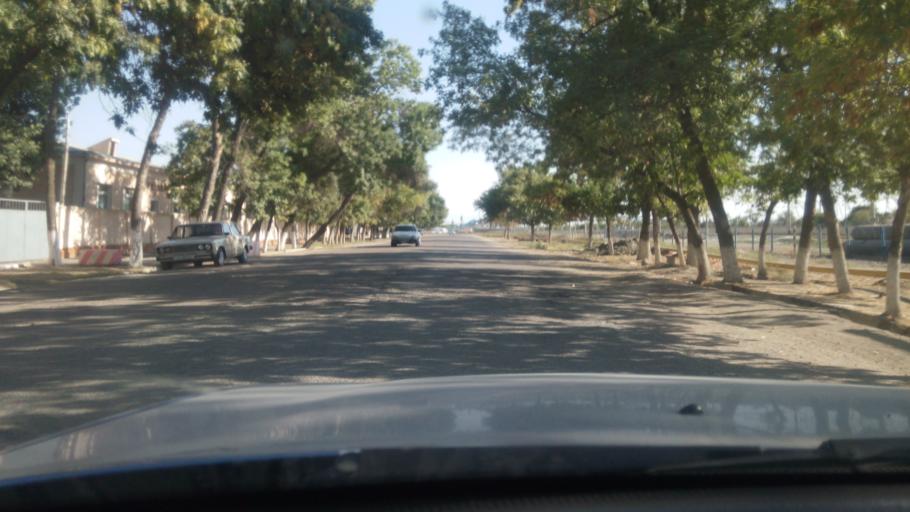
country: UZ
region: Sirdaryo
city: Guliston
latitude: 40.5019
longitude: 68.7636
